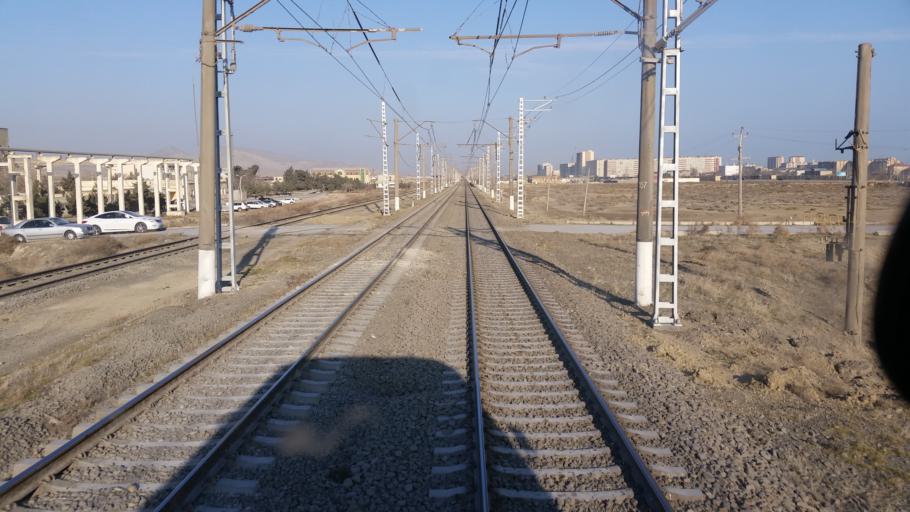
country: AZ
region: Baki
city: Korgoz
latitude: 40.2230
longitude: 49.5597
